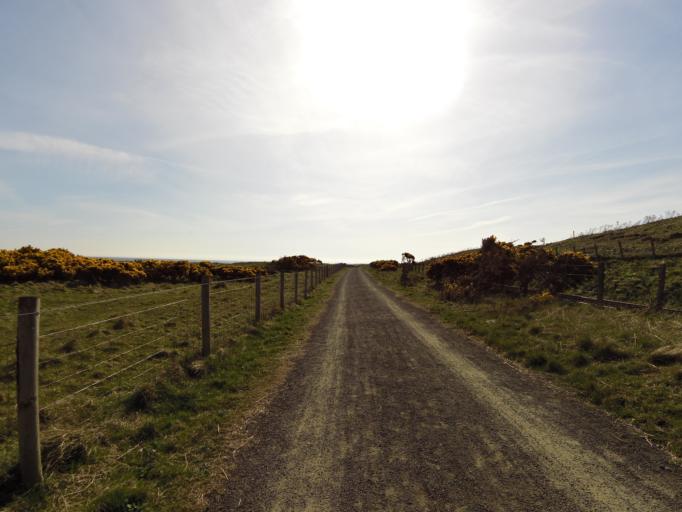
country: GB
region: Scotland
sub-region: Angus
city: Arbroath
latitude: 56.5270
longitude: -2.6402
